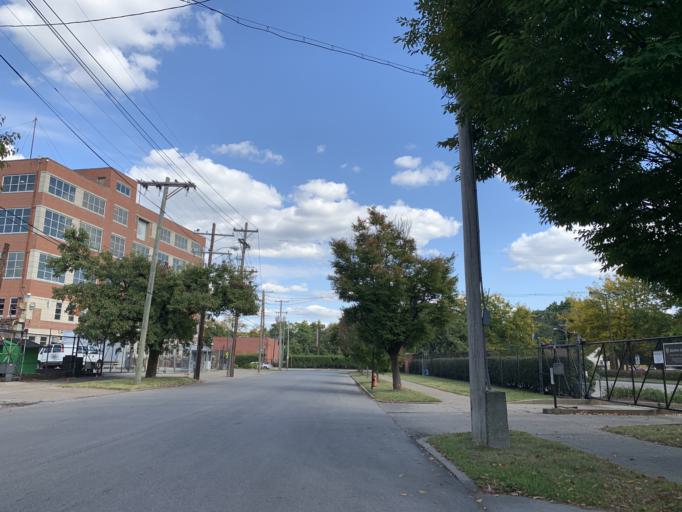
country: US
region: Kentucky
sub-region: Jefferson County
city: Louisville
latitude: 38.2437
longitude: -85.7855
